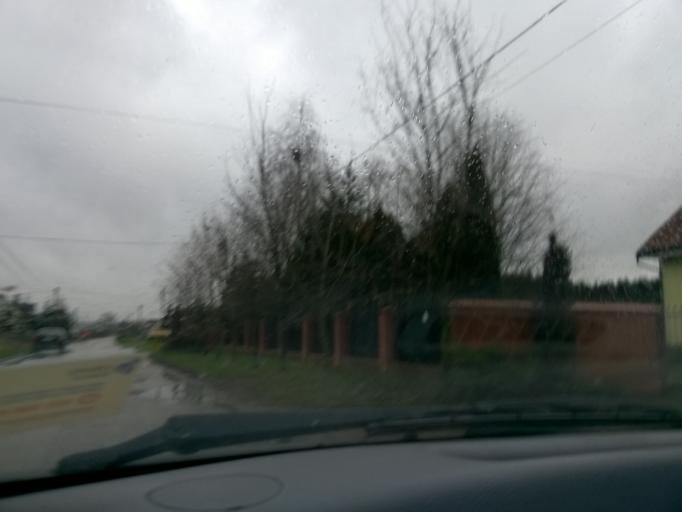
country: PL
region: Kujawsko-Pomorskie
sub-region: Powiat nakielski
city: Naklo nad Notecia
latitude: 53.1344
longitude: 17.5604
